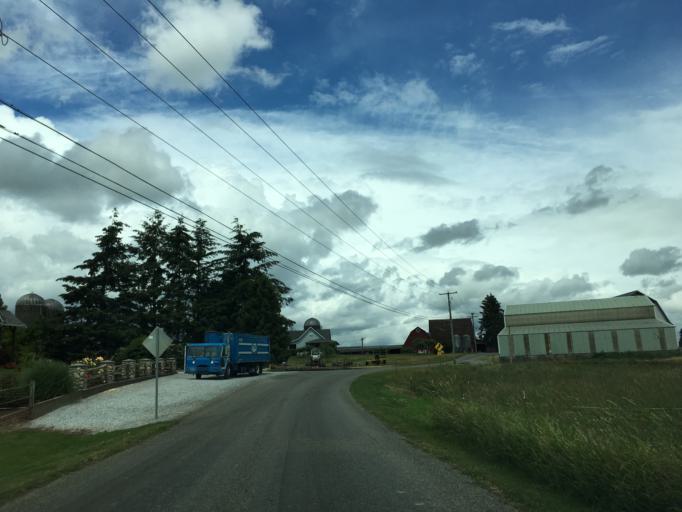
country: US
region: Washington
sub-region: Whatcom County
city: Lynden
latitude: 48.9295
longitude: -122.4962
